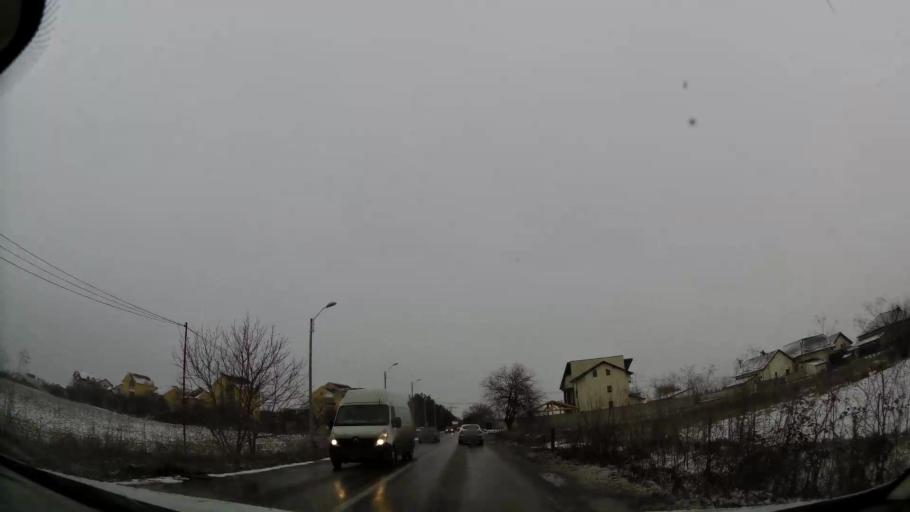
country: RO
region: Dambovita
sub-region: Comuna Ulmi
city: Ulmi
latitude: 44.9009
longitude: 25.5011
